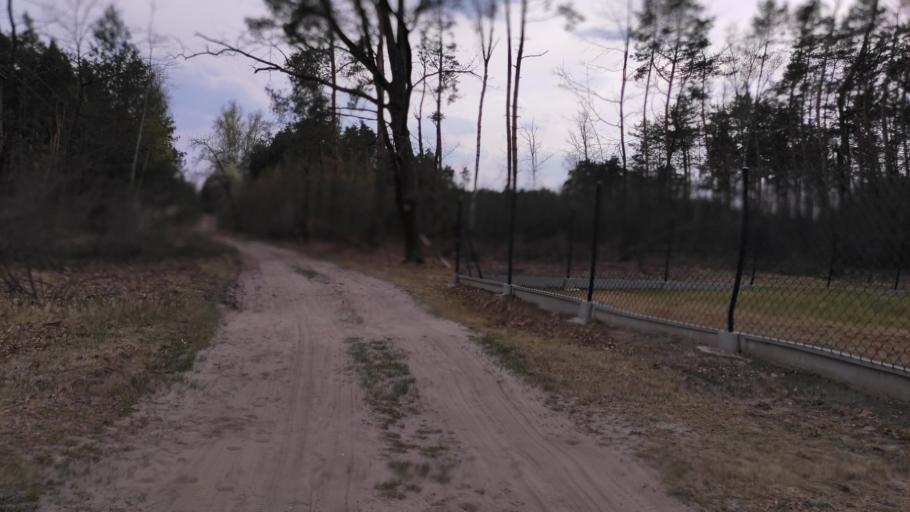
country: PL
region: Masovian Voivodeship
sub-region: Powiat grojecki
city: Warka
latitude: 51.7690
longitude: 21.1981
